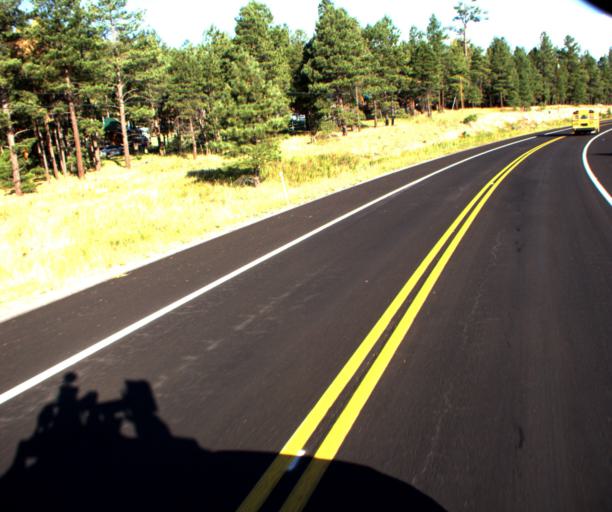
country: US
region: Arizona
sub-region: Apache County
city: Eagar
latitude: 33.8284
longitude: -109.1139
